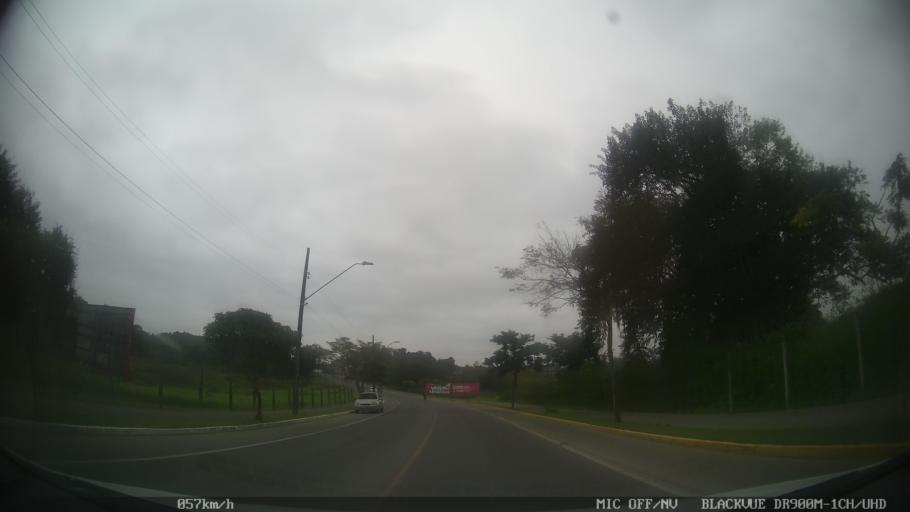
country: BR
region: Santa Catarina
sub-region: Joinville
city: Joinville
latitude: -26.3522
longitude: -48.8387
